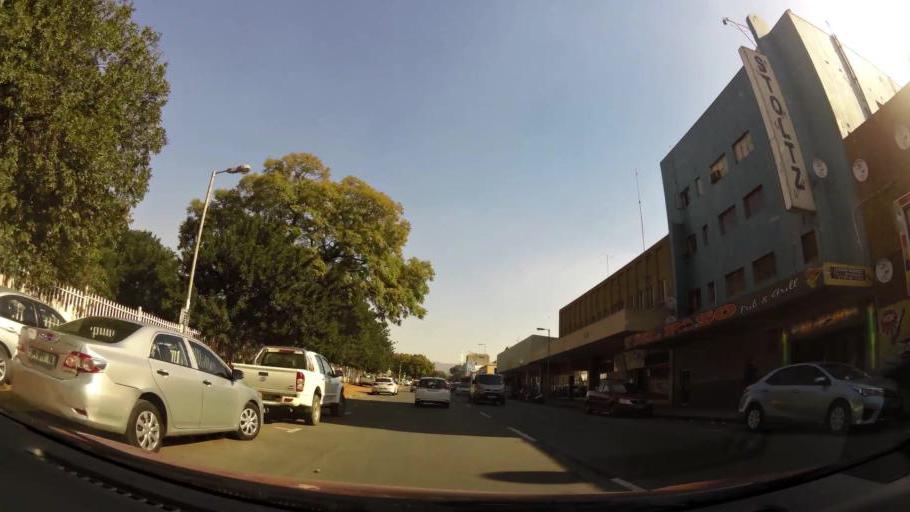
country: ZA
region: North-West
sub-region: Bojanala Platinum District Municipality
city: Rustenburg
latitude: -25.6709
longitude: 27.2455
